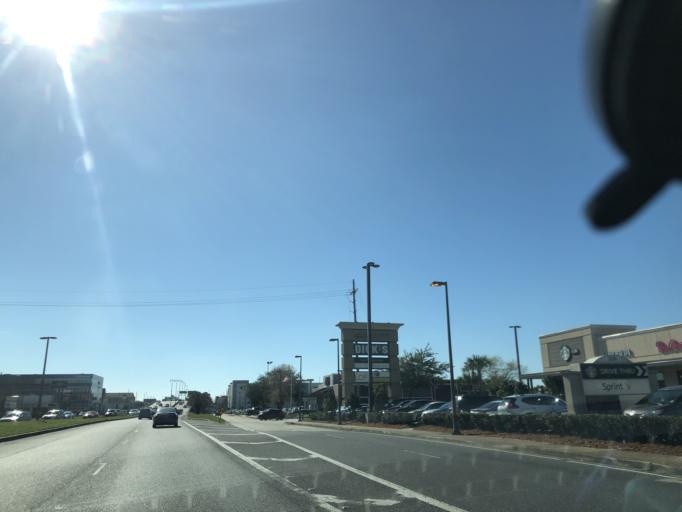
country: US
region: Louisiana
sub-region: Jefferson Parish
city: Metairie
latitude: 30.0086
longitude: -90.1553
